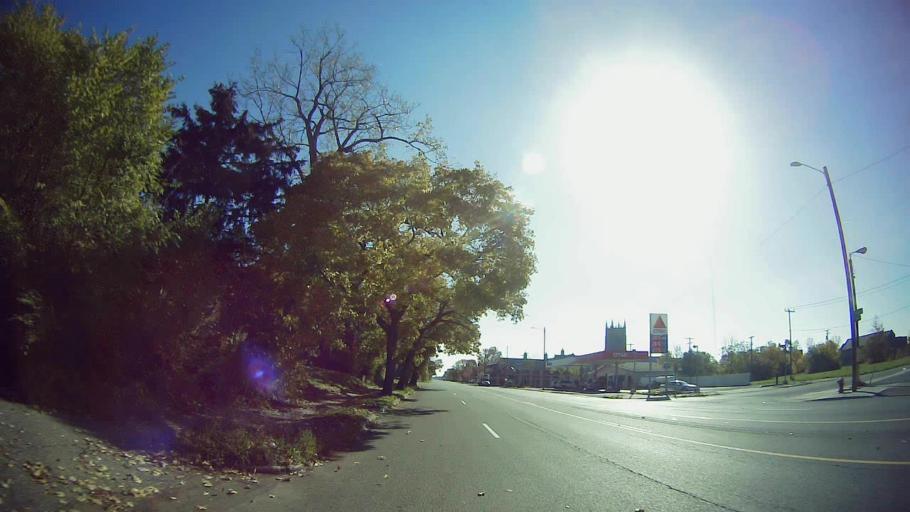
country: US
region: Michigan
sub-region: Wayne County
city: Highland Park
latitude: 42.3784
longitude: -83.1119
